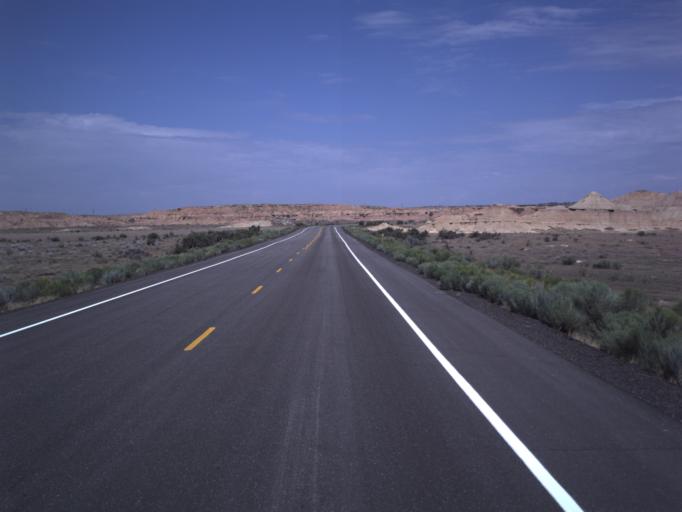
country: US
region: Utah
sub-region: Uintah County
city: Naples
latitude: 40.1183
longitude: -109.2507
